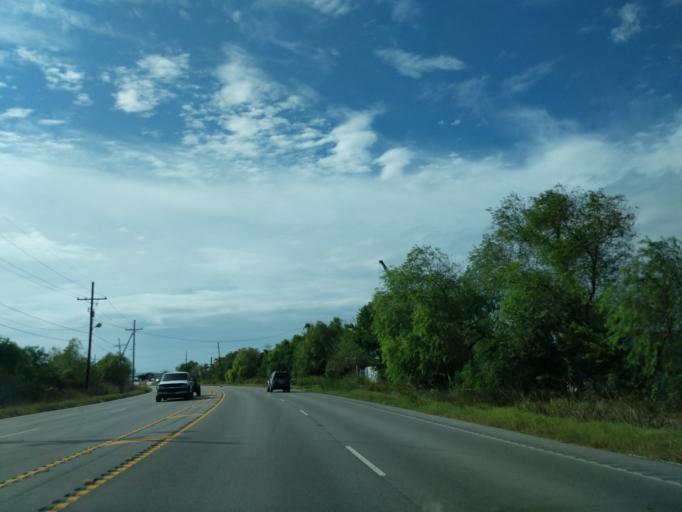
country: US
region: Louisiana
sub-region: Saint Tammany Parish
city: Eden Isle
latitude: 30.0763
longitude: -89.8439
